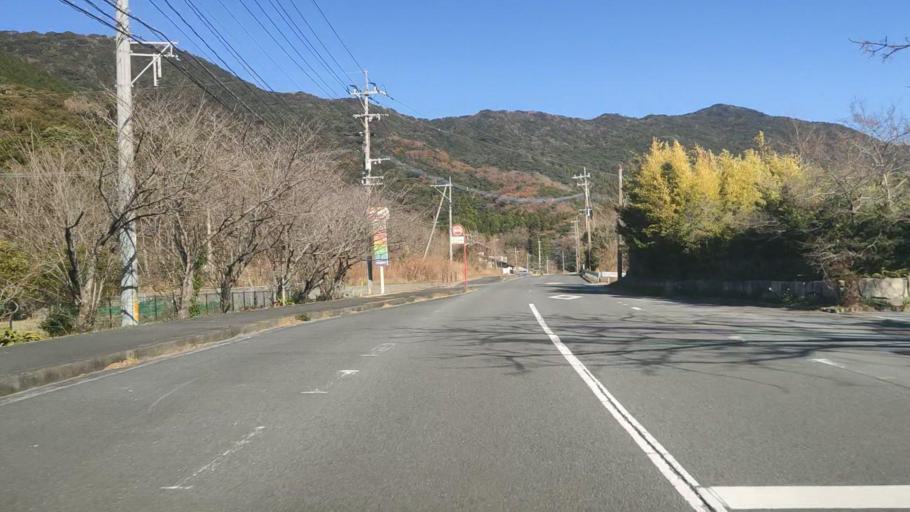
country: JP
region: Oita
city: Saiki
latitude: 32.8029
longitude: 131.9438
